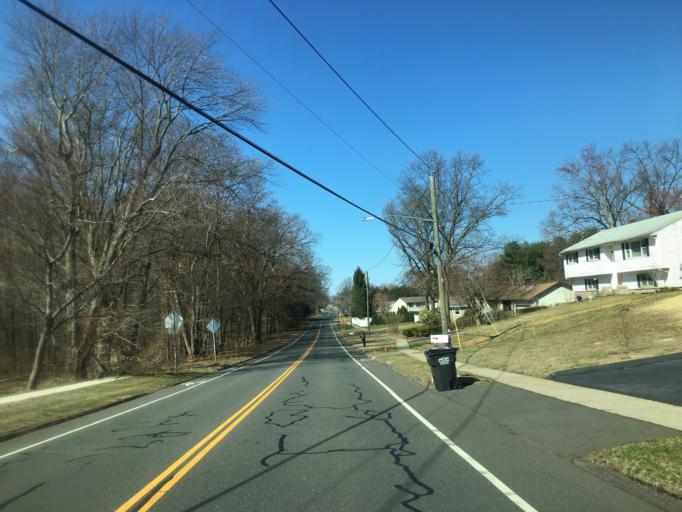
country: US
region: Connecticut
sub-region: Hartford County
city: East Hartford
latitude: 41.8069
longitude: -72.5964
